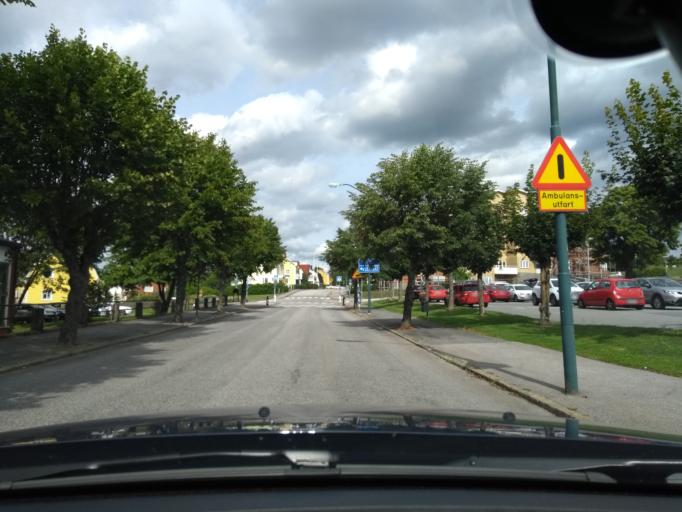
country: SE
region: Kalmar
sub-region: Vimmerby Kommun
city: Vimmerby
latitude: 57.6685
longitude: 15.8577
